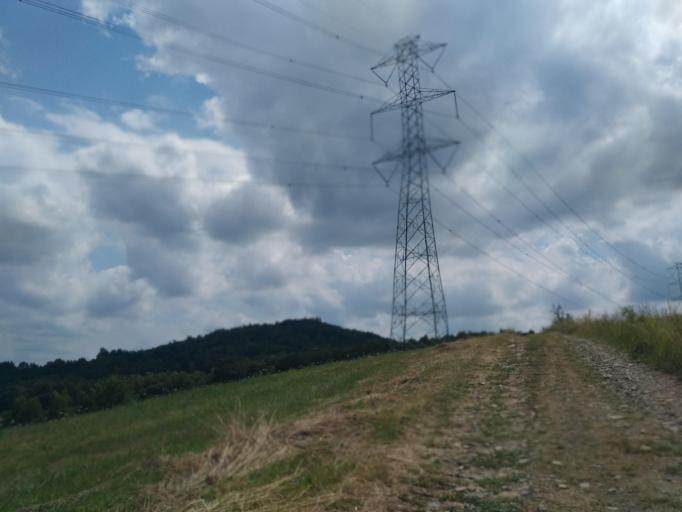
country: PL
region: Subcarpathian Voivodeship
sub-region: Powiat krosnienski
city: Iwonicz-Zdroj
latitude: 49.5898
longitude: 21.7759
